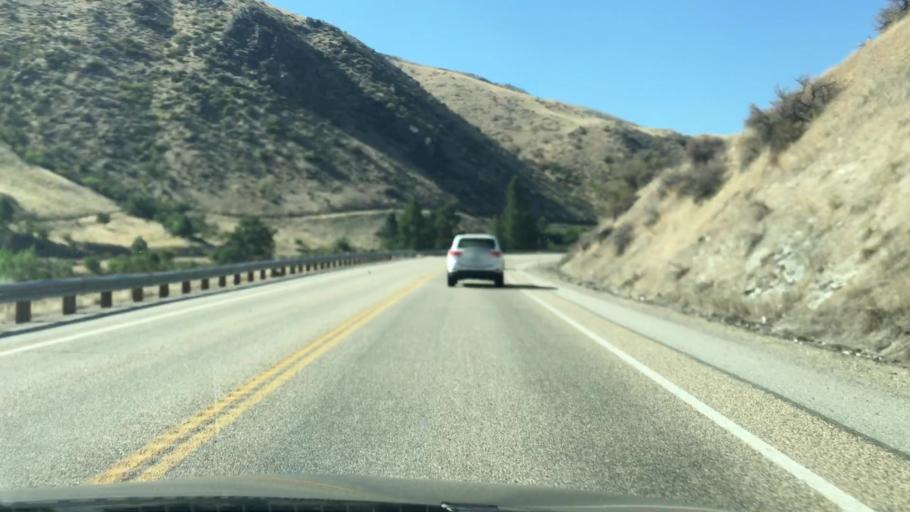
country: US
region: Idaho
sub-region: Ada County
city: Eagle
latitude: 43.9416
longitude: -116.1956
